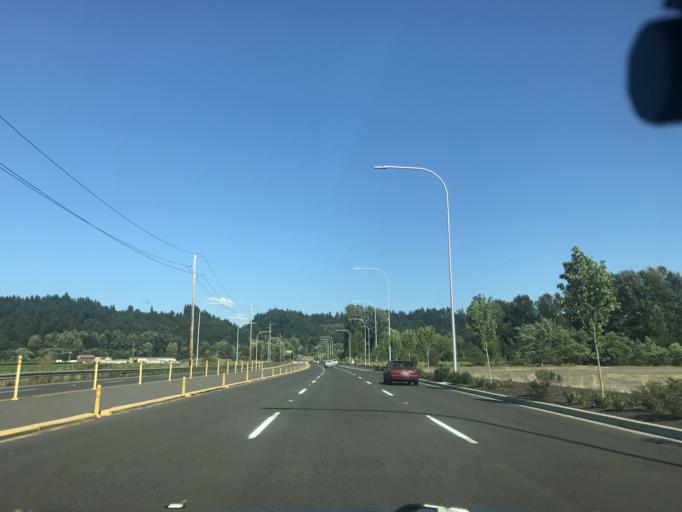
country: US
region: Washington
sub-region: King County
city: Kent
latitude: 47.3536
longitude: -122.2236
